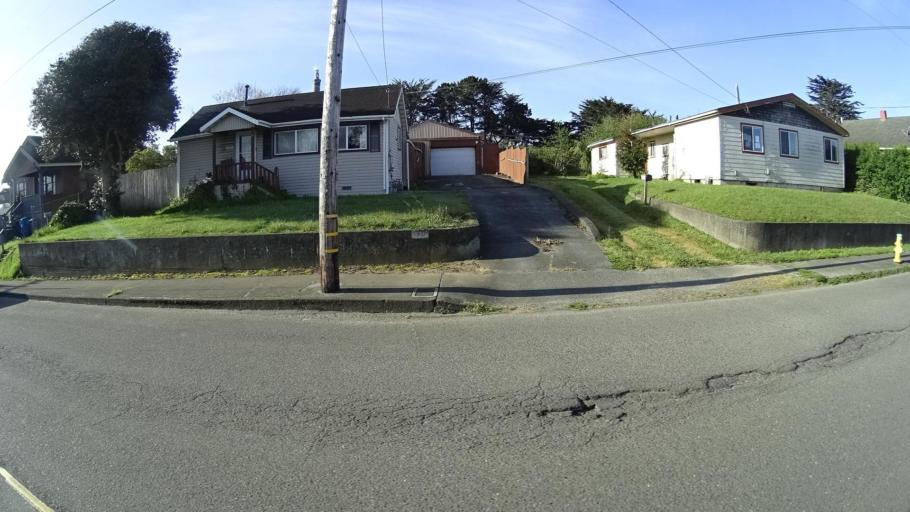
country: US
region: California
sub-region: Humboldt County
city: Bayview
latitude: 40.7742
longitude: -124.1862
